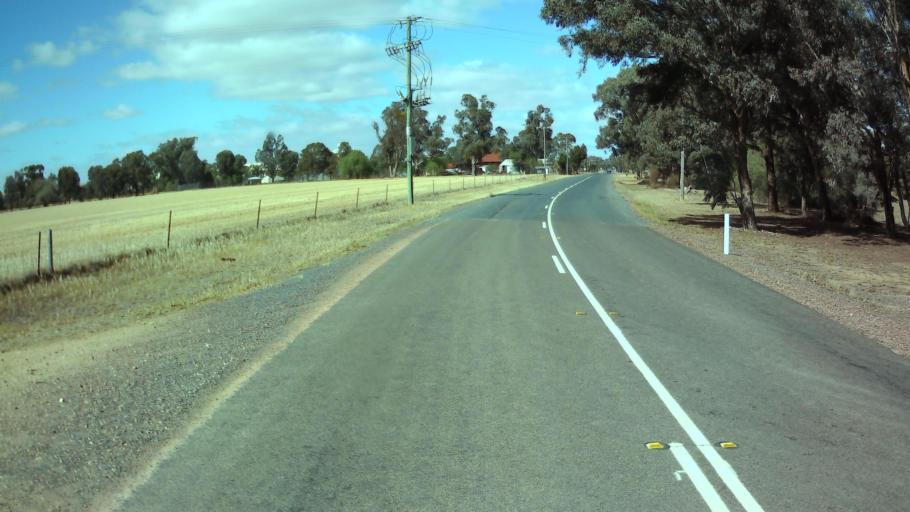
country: AU
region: New South Wales
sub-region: Weddin
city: Grenfell
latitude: -33.9926
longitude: 148.4077
